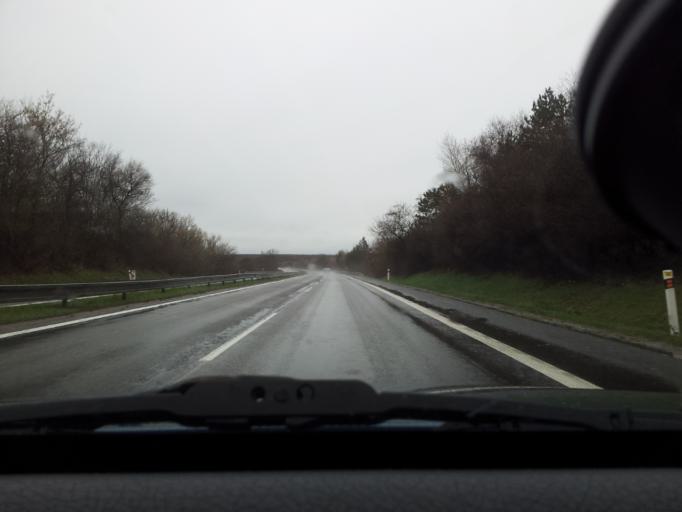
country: SK
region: Nitriansky
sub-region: Okres Nitra
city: Nitra
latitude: 48.3239
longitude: 17.9814
